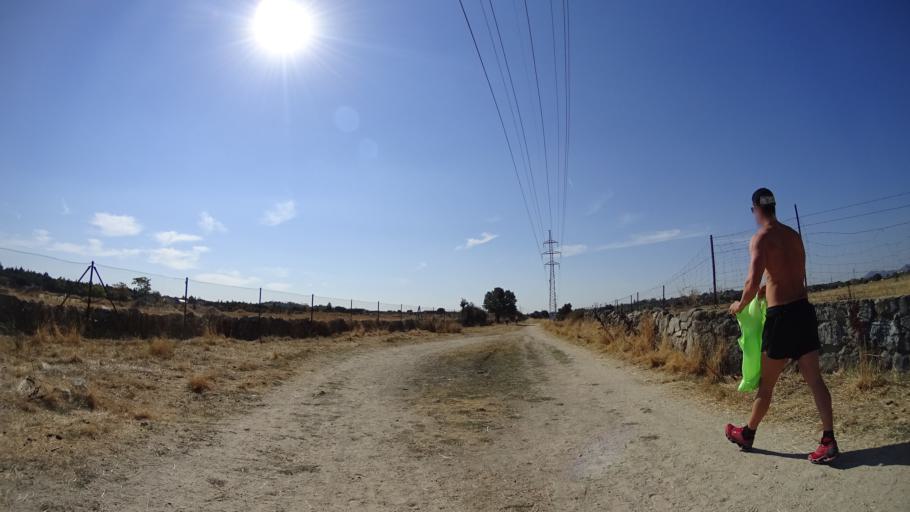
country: ES
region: Madrid
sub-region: Provincia de Madrid
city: Collado-Villalba
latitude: 40.6190
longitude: -4.0202
